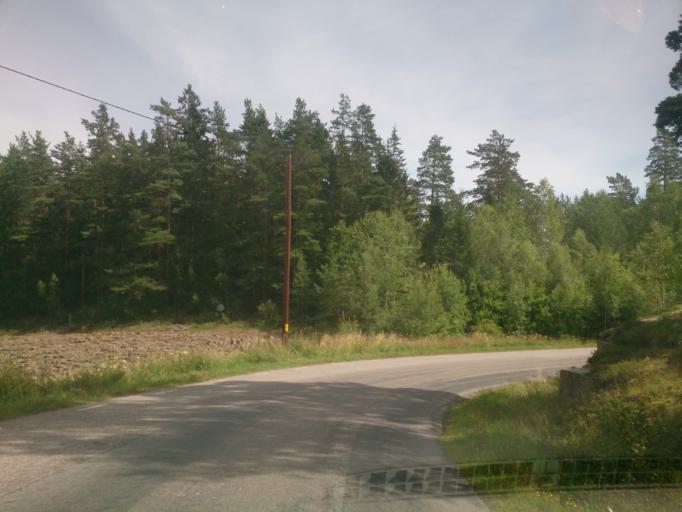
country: SE
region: OEstergoetland
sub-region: Valdemarsviks Kommun
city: Gusum
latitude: 58.2859
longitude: 16.5281
